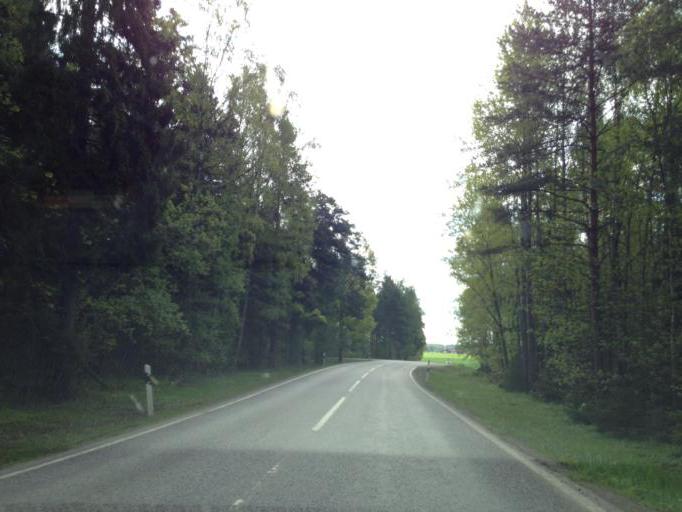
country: SE
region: Soedermanland
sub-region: Nykopings Kommun
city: Svalsta
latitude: 58.8646
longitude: 16.9076
